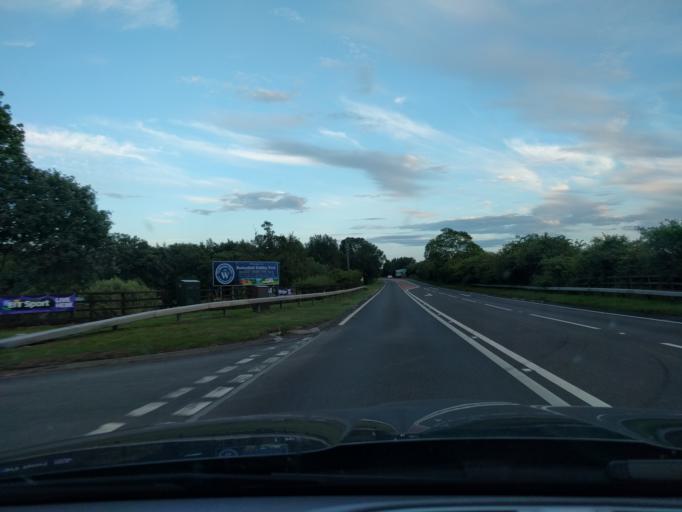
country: GB
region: England
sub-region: Northumberland
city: Felton
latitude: 55.2700
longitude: -1.7209
